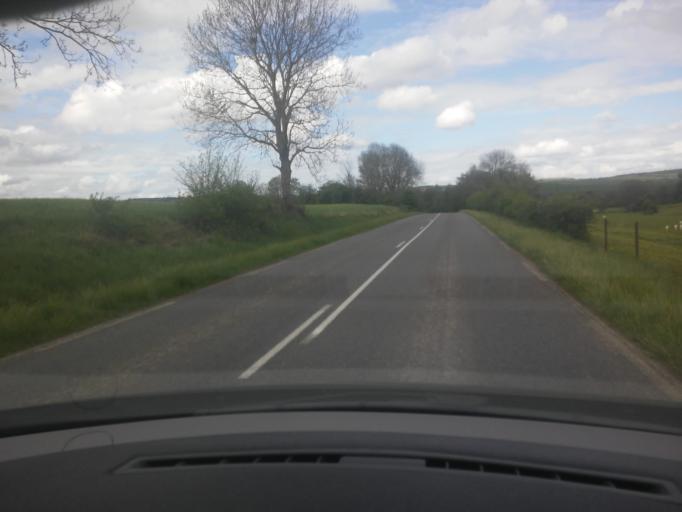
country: FR
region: Lorraine
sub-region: Departement de Meurthe-et-Moselle
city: Pierrepont
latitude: 49.4191
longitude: 5.6693
